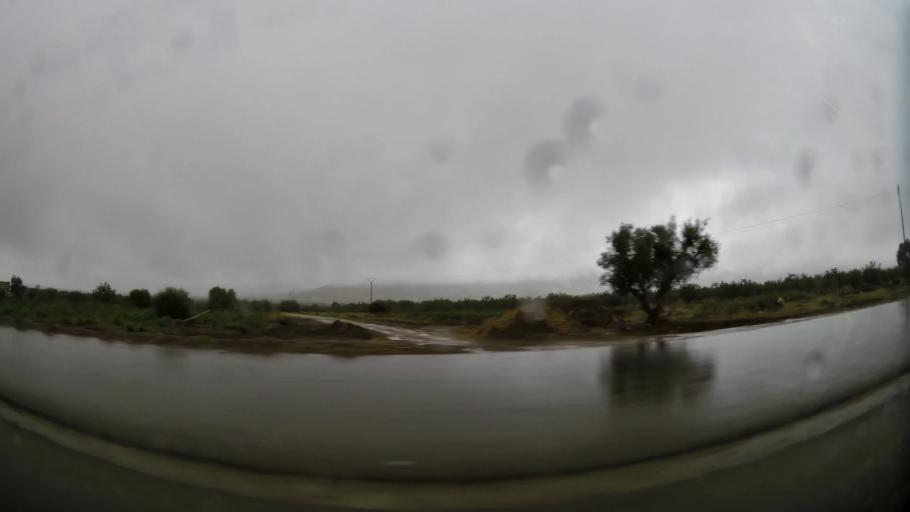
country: MA
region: Oriental
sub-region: Nador
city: Midar
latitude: 34.8508
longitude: -3.7218
